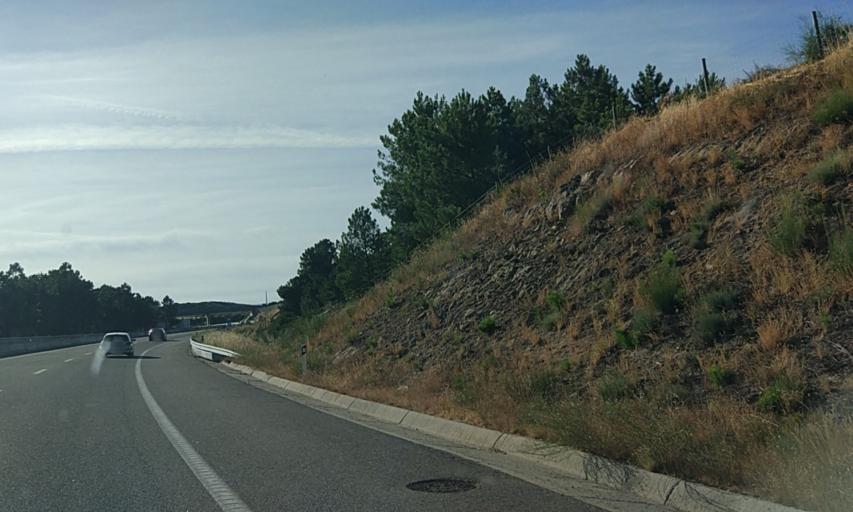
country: PT
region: Vila Real
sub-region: Murca
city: Murca
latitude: 41.3864
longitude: -7.5020
